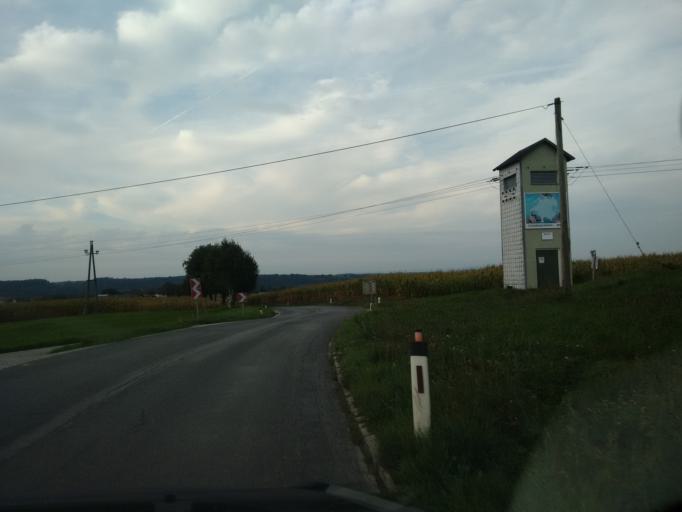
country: AT
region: Upper Austria
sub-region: Politischer Bezirk Steyr-Land
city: Pfarrkirchen bei Bad Hall
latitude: 48.0486
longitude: 14.1786
